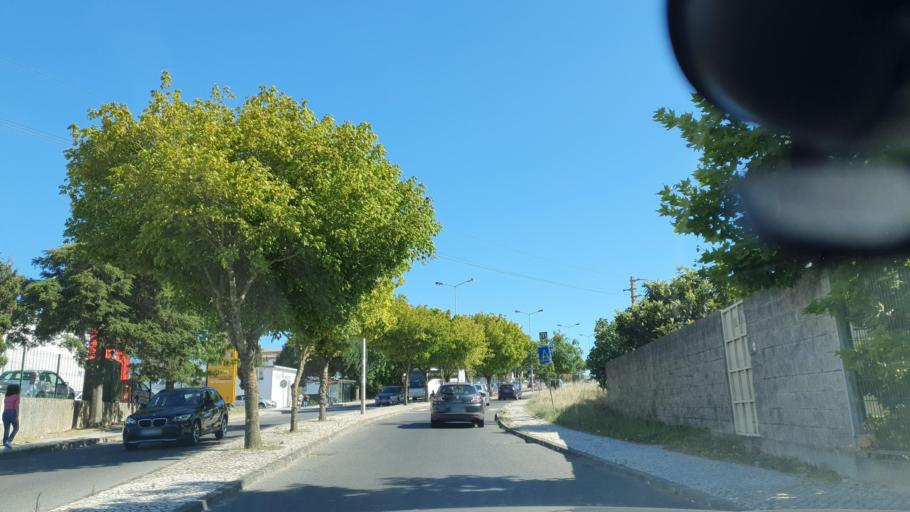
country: PT
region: Lisbon
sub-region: Sintra
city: Cacem
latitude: 38.7687
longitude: -9.2791
